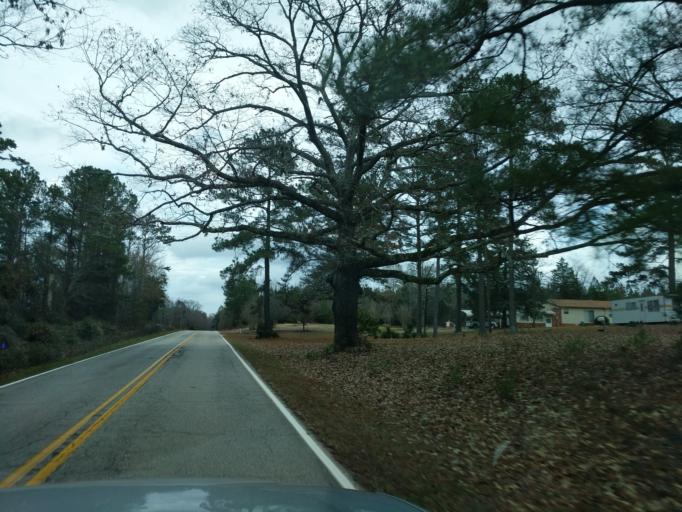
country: US
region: South Carolina
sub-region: Greenwood County
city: Ware Shoals
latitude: 34.4012
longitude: -82.1363
